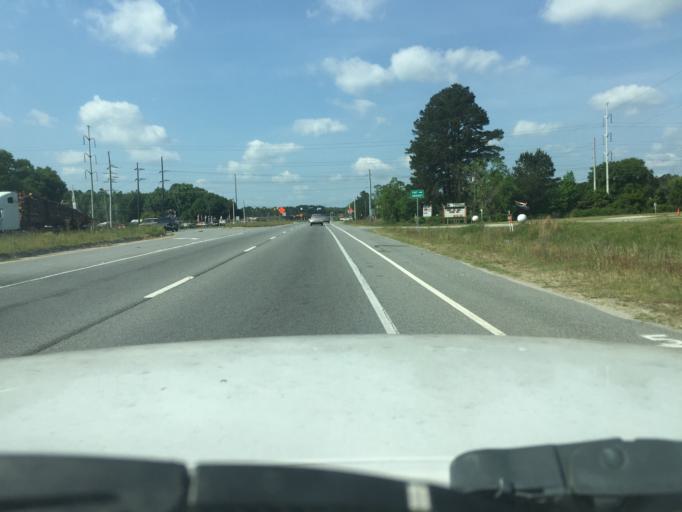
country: US
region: Georgia
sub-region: Chatham County
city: Georgetown
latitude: 32.0043
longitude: -81.2440
